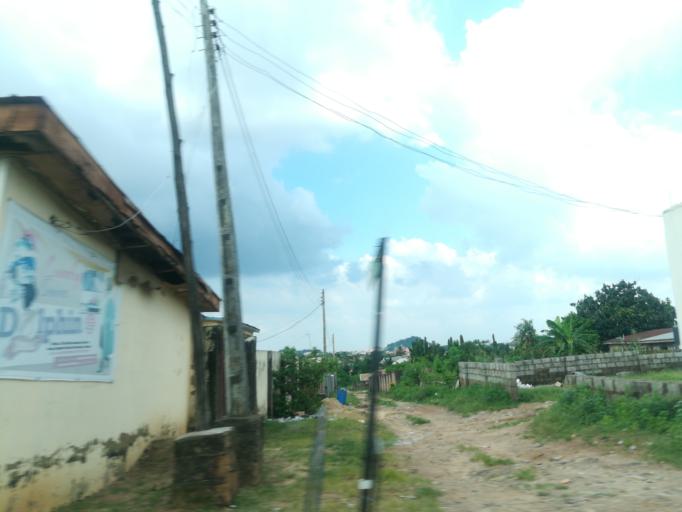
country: NG
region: Oyo
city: Ibadan
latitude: 7.4033
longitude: 3.8337
